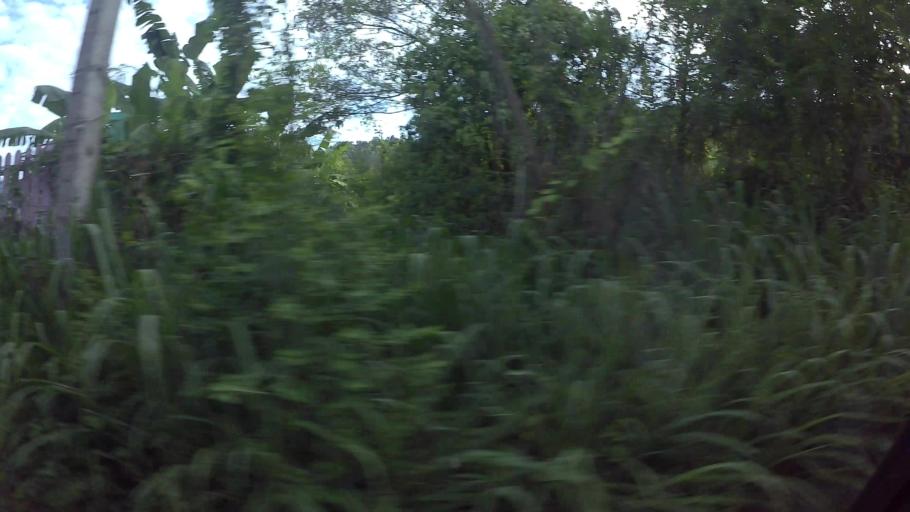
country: TH
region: Chon Buri
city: Sattahip
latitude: 12.6923
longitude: 100.9243
